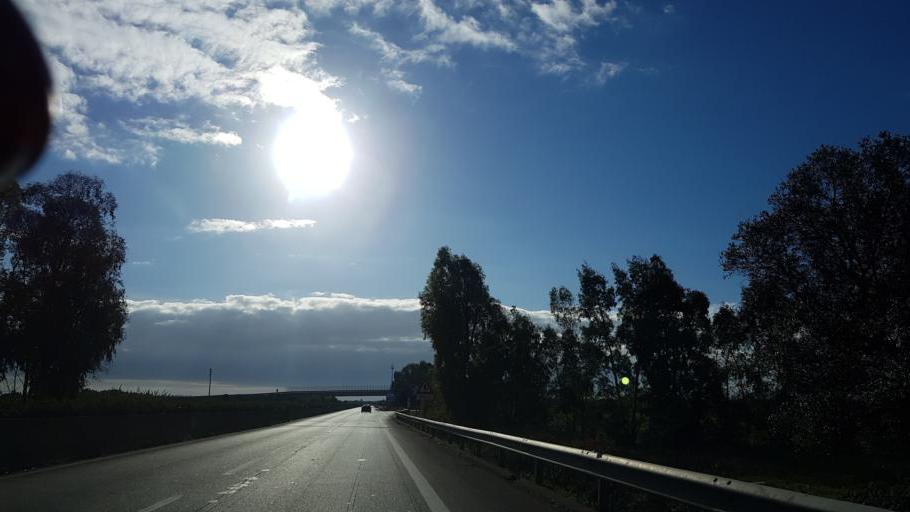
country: IT
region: Apulia
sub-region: Provincia di Brindisi
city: Tuturano
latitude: 40.5571
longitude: 17.9920
